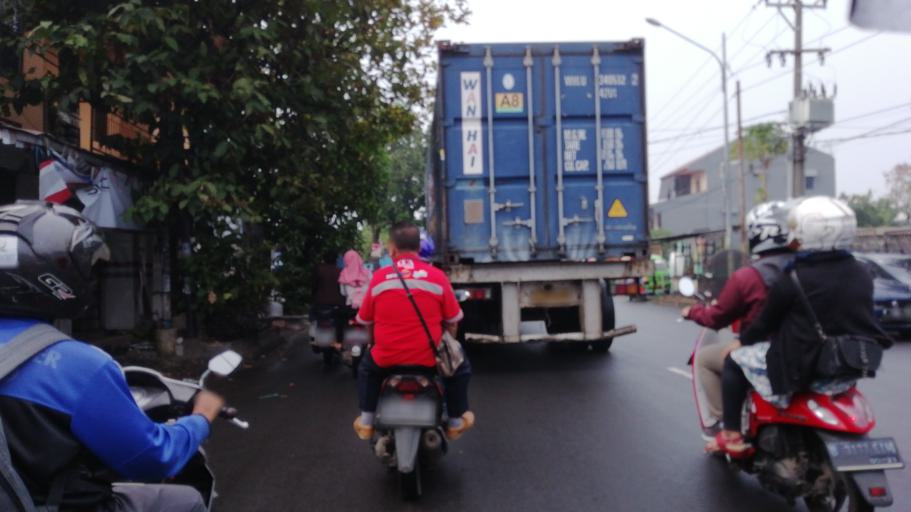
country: ID
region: West Java
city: Bogor
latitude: -6.5443
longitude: 106.8058
